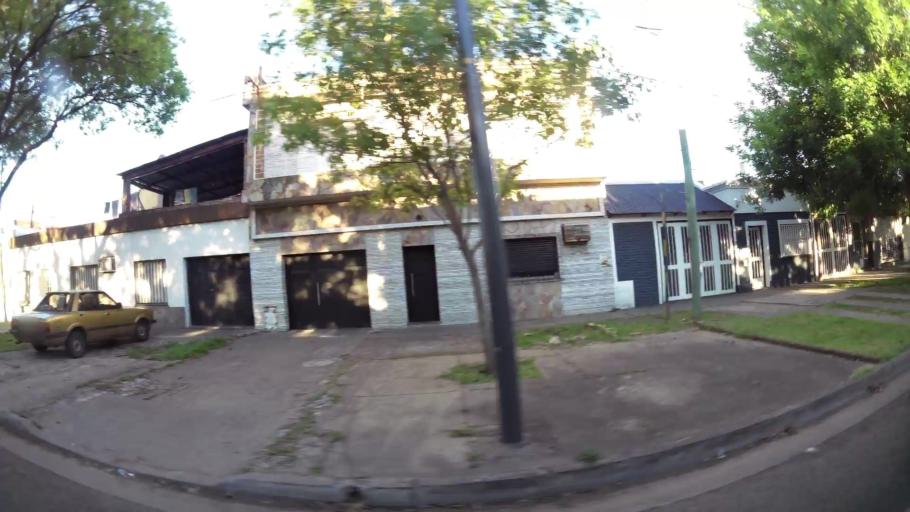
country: AR
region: Santa Fe
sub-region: Departamento de Rosario
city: Rosario
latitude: -32.9722
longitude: -60.6699
